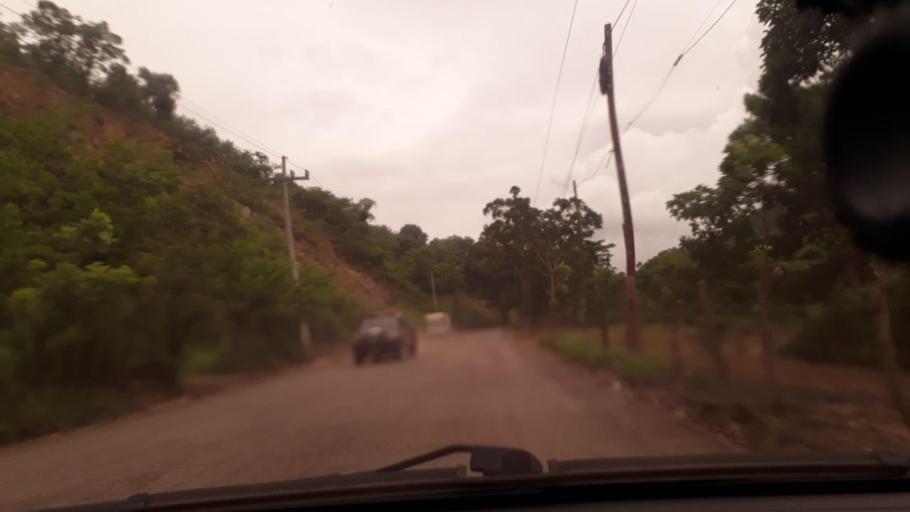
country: GT
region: Chiquimula
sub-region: Municipio de San Juan Ermita
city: San Juan Ermita
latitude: 14.7537
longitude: -89.4457
